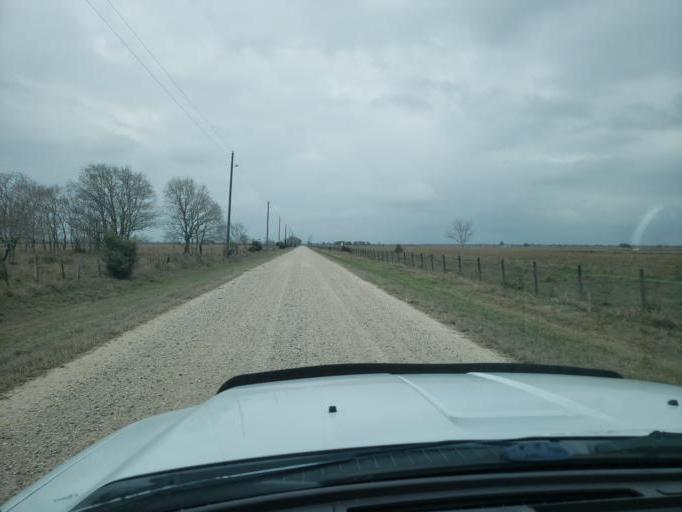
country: US
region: Texas
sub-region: Fort Bend County
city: Needville
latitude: 29.3626
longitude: -95.7319
